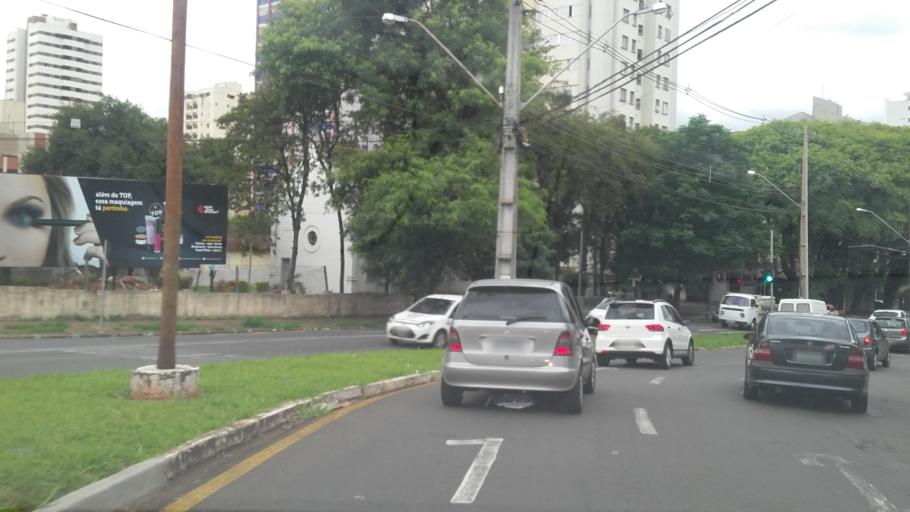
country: BR
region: Parana
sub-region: Londrina
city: Londrina
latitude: -23.3060
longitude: -51.1708
